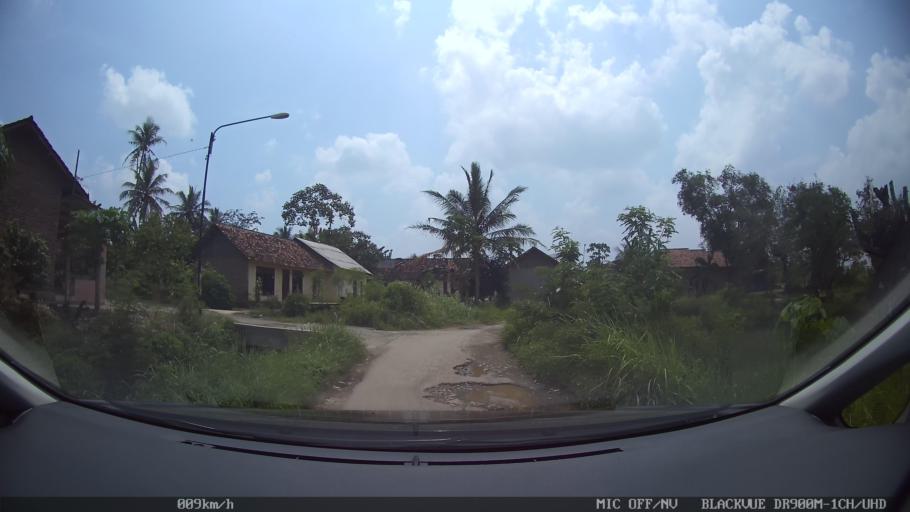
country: ID
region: Lampung
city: Pringsewu
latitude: -5.3397
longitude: 104.9780
